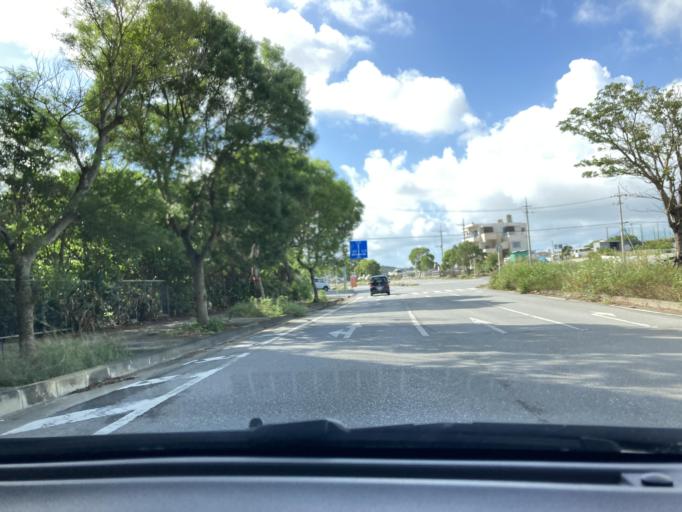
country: JP
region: Okinawa
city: Tomigusuku
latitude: 26.1811
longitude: 127.7196
